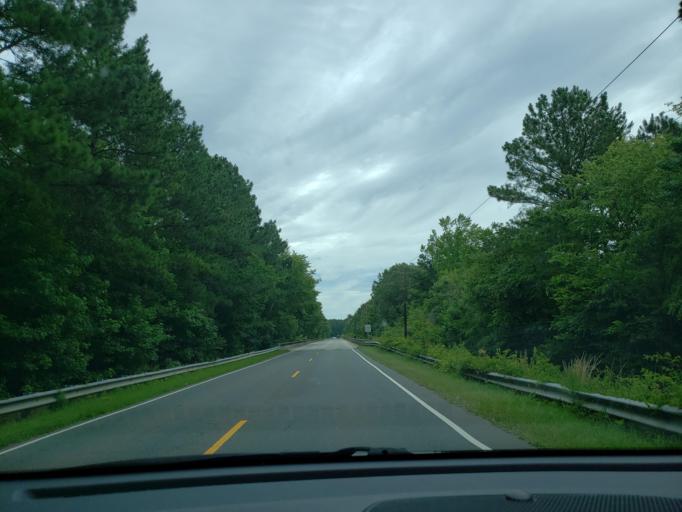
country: US
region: North Carolina
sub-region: Orange County
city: Chapel Hill
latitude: 35.8603
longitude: -79.0110
